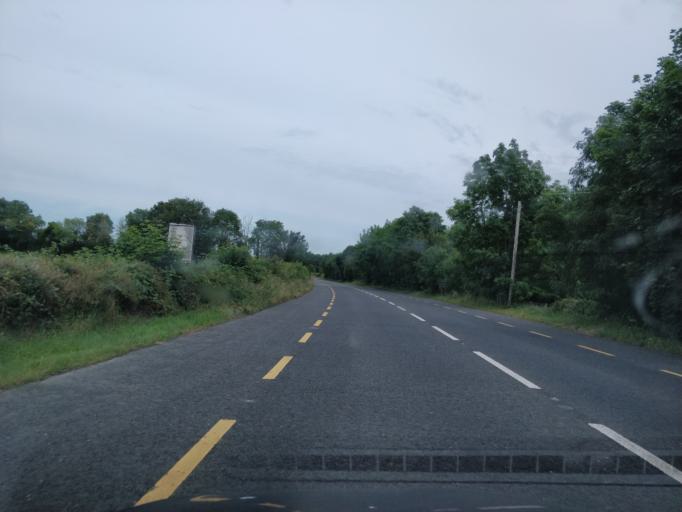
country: IE
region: Leinster
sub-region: Uibh Fhaili
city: Ferbane
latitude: 53.1688
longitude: -7.7516
